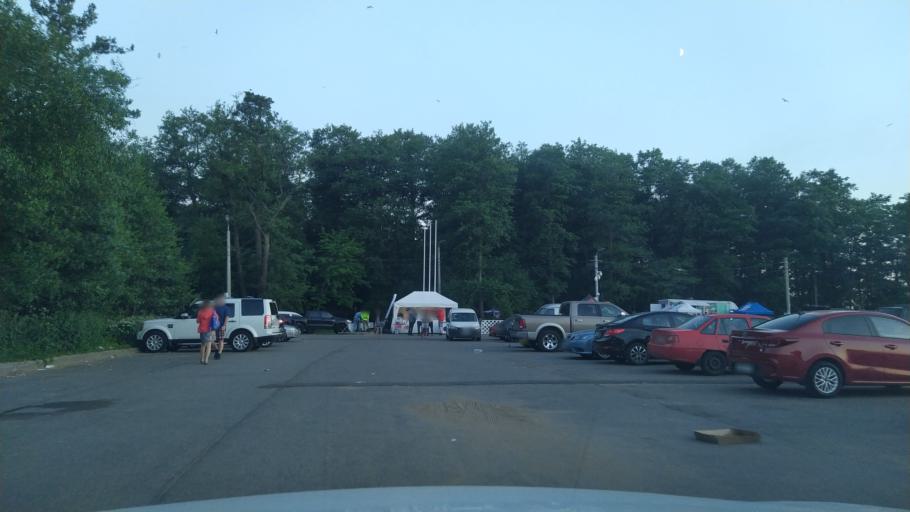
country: RU
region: St.-Petersburg
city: Sestroretsk
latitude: 60.0938
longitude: 29.9407
